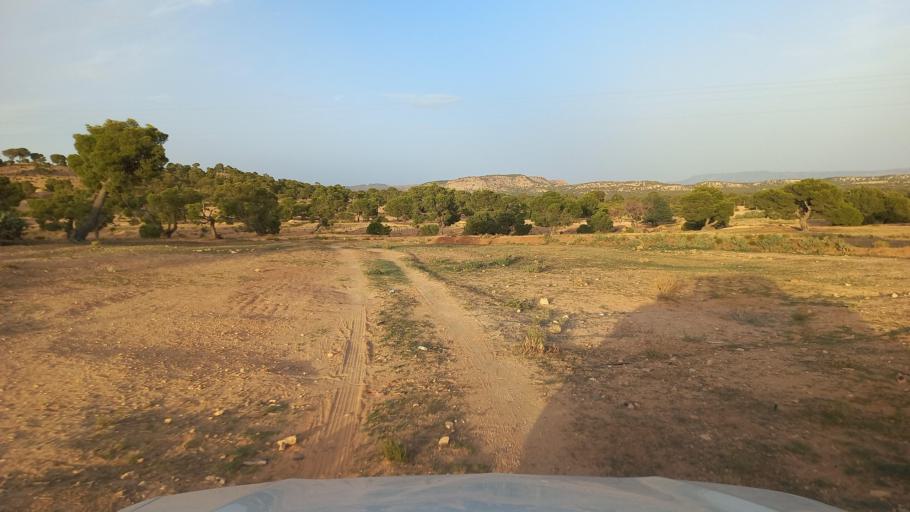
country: TN
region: Al Qasrayn
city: Sbiba
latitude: 35.4140
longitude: 8.9091
